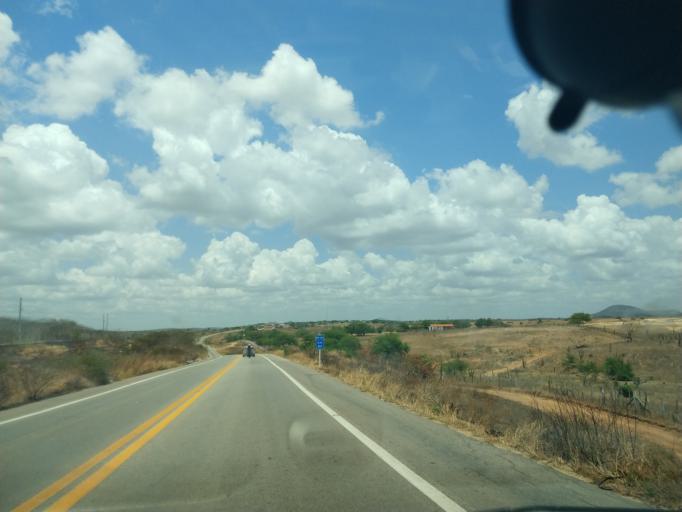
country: BR
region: Rio Grande do Norte
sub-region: Tangara
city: Tangara
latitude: -6.1835
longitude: -35.7749
